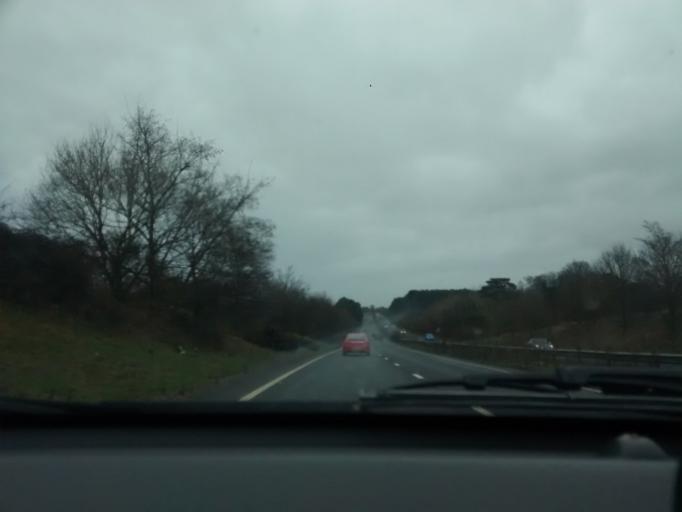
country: GB
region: England
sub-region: Suffolk
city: Kesgrave
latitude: 52.0415
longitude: 1.2642
